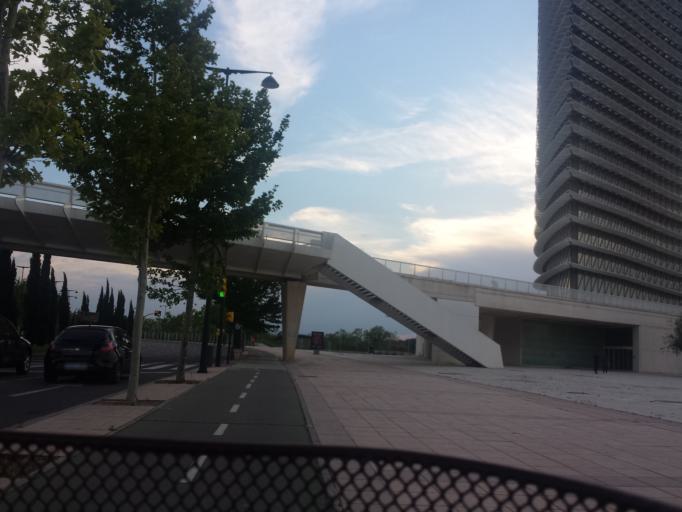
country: ES
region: Aragon
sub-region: Provincia de Zaragoza
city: Almozara
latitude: 41.6702
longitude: -0.9062
